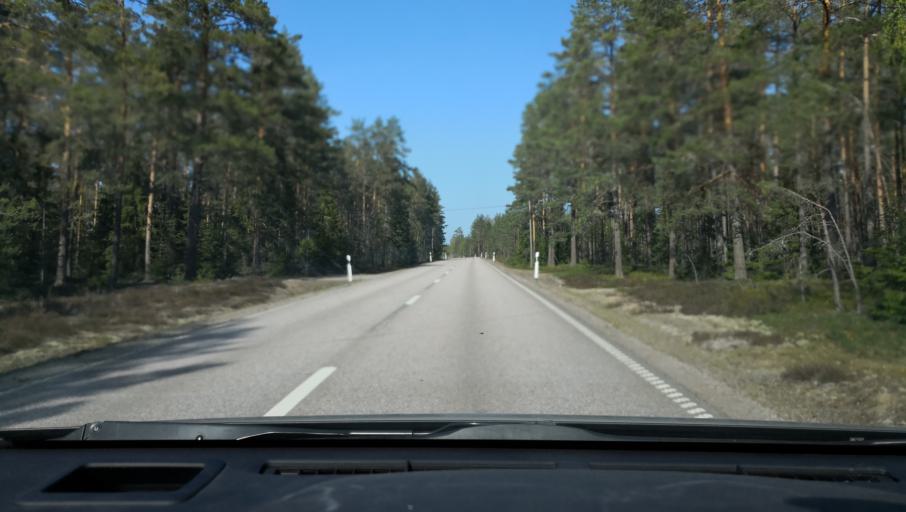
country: SE
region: Uppsala
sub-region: Heby Kommun
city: Tarnsjo
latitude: 60.0588
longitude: 16.8682
